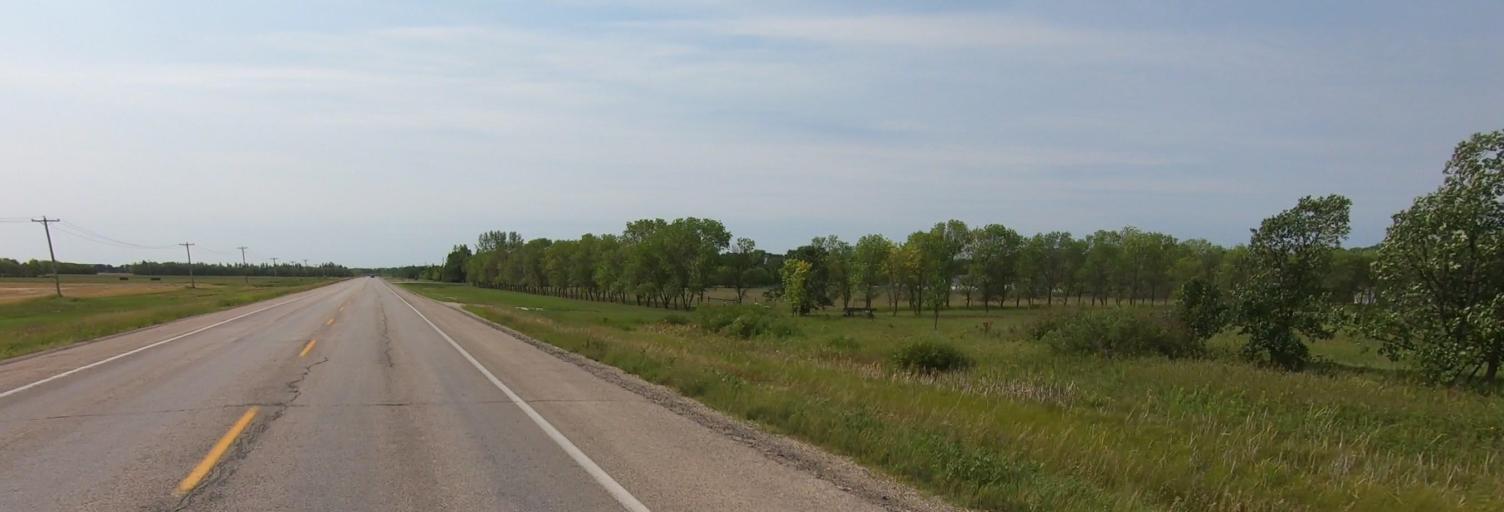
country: CA
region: Manitoba
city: Niverville
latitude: 49.6449
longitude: -97.1044
